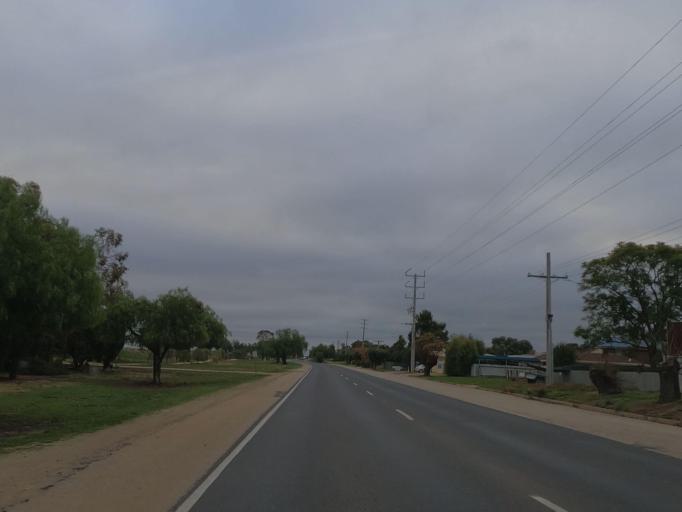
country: AU
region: Victoria
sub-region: Swan Hill
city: Swan Hill
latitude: -35.4596
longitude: 143.6324
